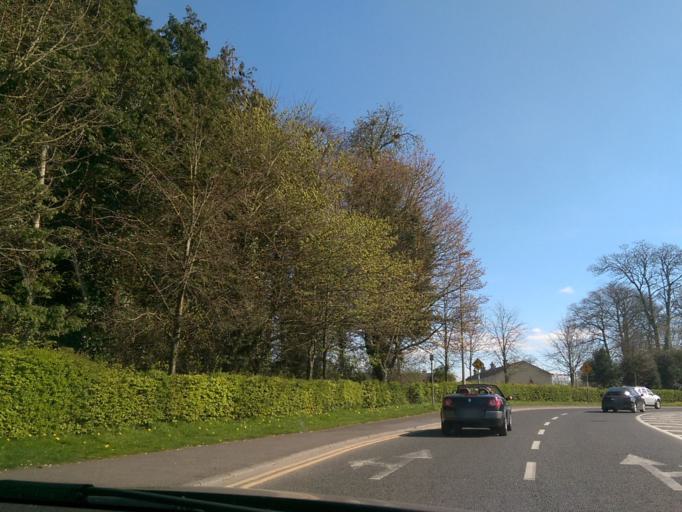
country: IE
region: Leinster
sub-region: Laois
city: Portlaoise
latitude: 53.0343
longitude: -7.2941
